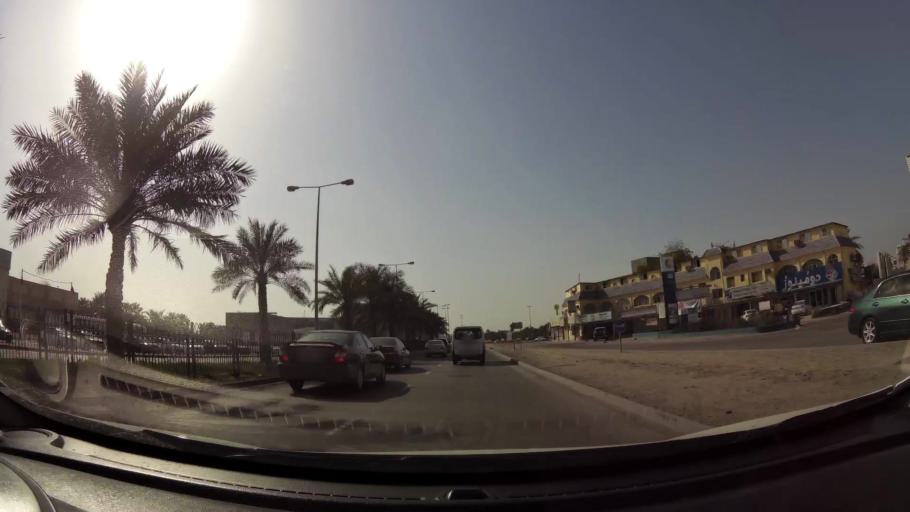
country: BH
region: Manama
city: Jidd Hafs
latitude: 26.2191
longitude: 50.5126
